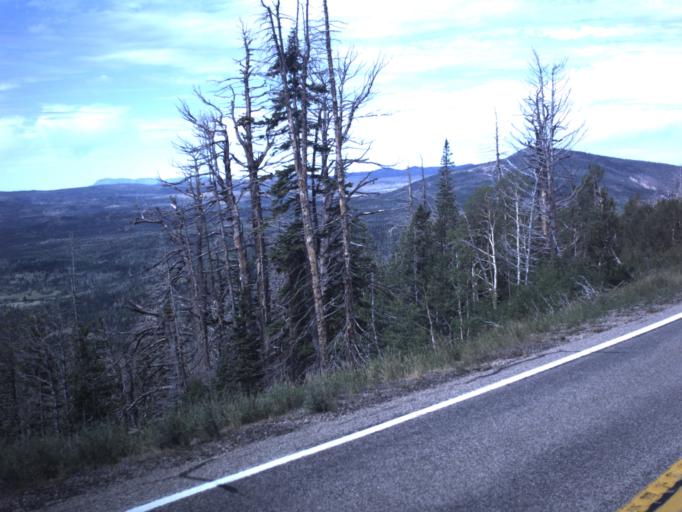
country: US
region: Utah
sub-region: Iron County
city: Cedar City
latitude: 37.5686
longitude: -112.8510
